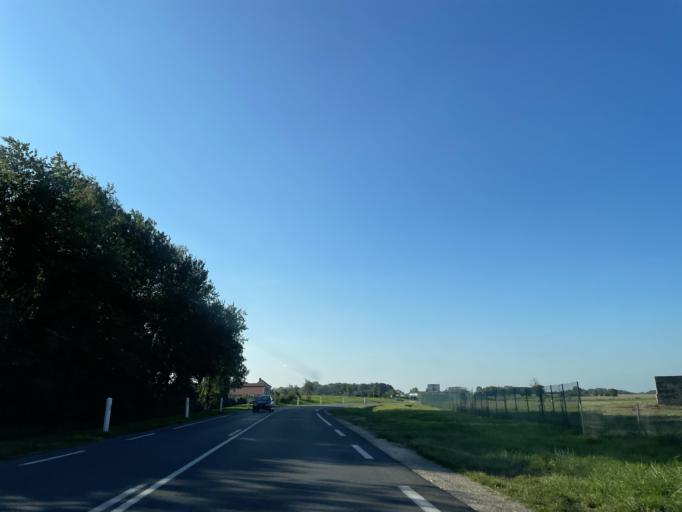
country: FR
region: Ile-de-France
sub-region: Departement de Seine-et-Marne
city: Pommeuse
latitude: 48.8352
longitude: 2.9918
